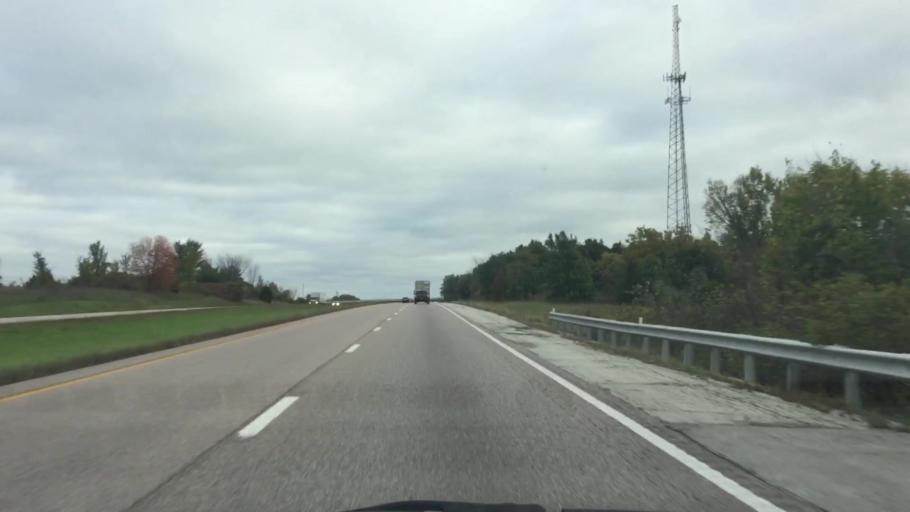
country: US
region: Missouri
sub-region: Clinton County
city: Lathrop
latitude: 39.4955
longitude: -94.2982
